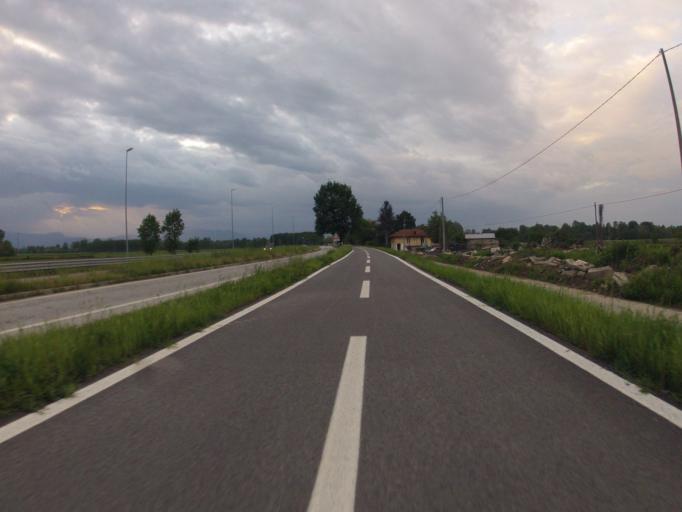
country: IT
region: Piedmont
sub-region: Provincia di Torino
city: Villafranca Piemonte
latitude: 44.8059
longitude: 7.5023
